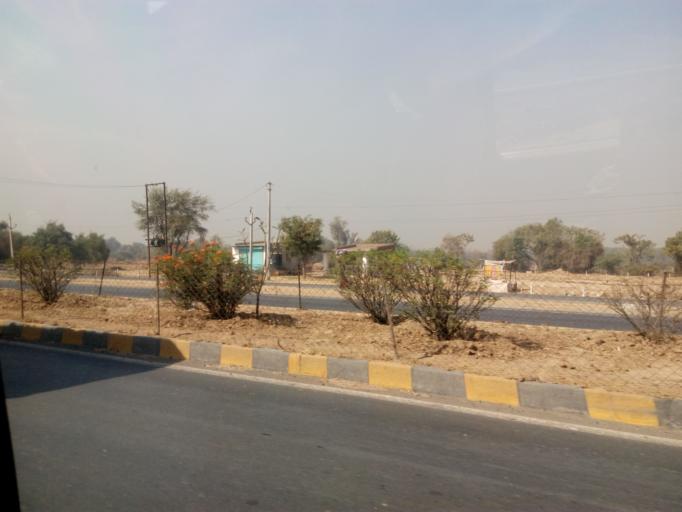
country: IN
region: Gujarat
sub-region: Ahmadabad
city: Sarkhej
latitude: 23.0169
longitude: 72.4789
